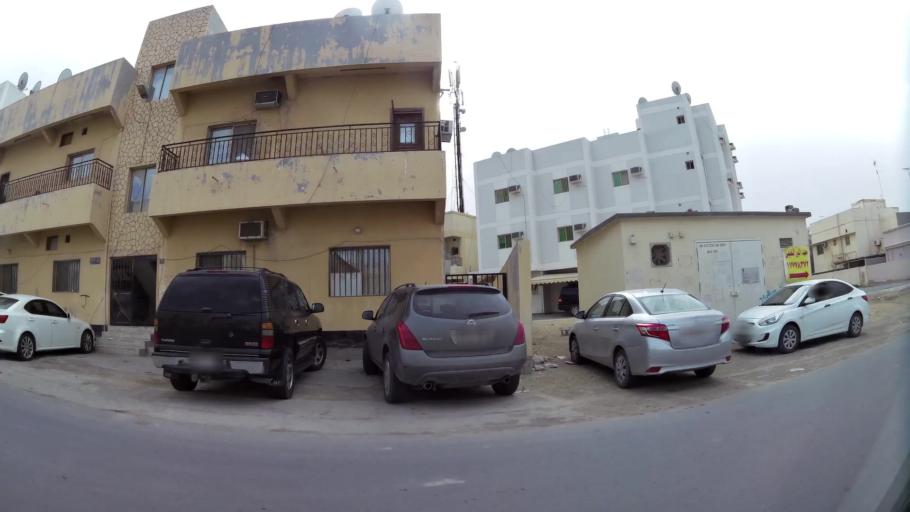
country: BH
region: Northern
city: Ar Rifa'
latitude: 26.1209
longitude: 50.5797
